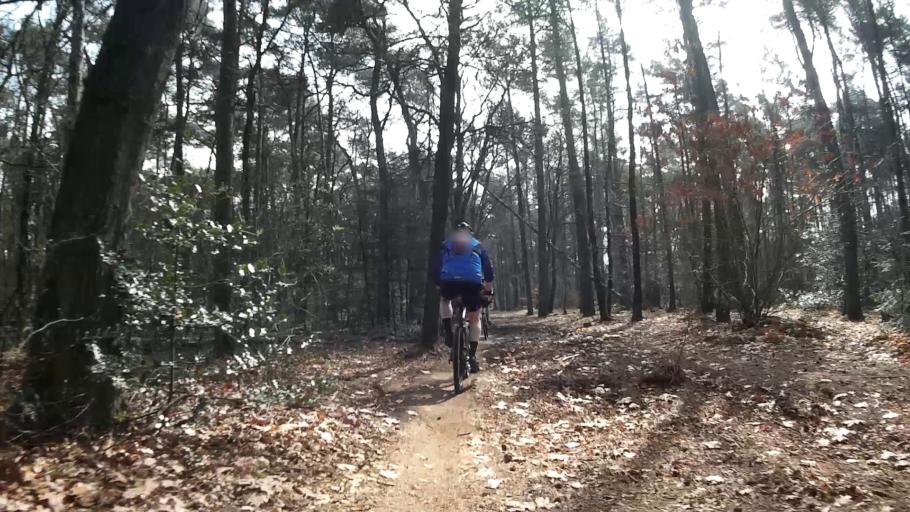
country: NL
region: Utrecht
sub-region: Gemeente Utrechtse Heuvelrug
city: Driebergen-Rijsenburg
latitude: 52.0926
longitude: 5.2947
